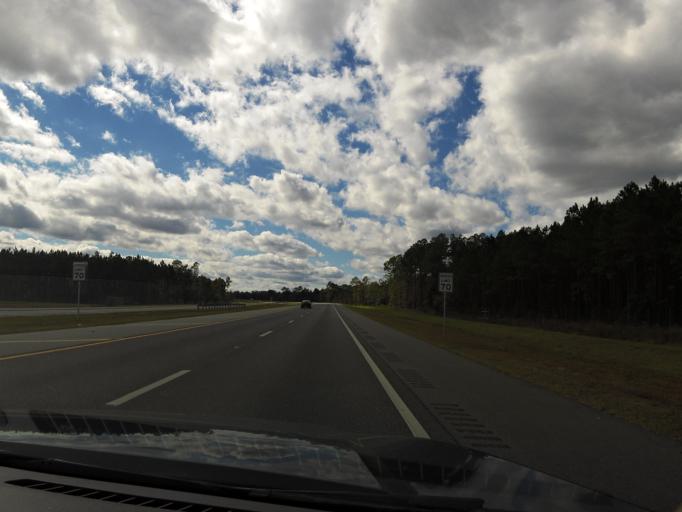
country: US
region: Florida
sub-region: Bradford County
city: Starke
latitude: 29.9867
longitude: -82.1083
